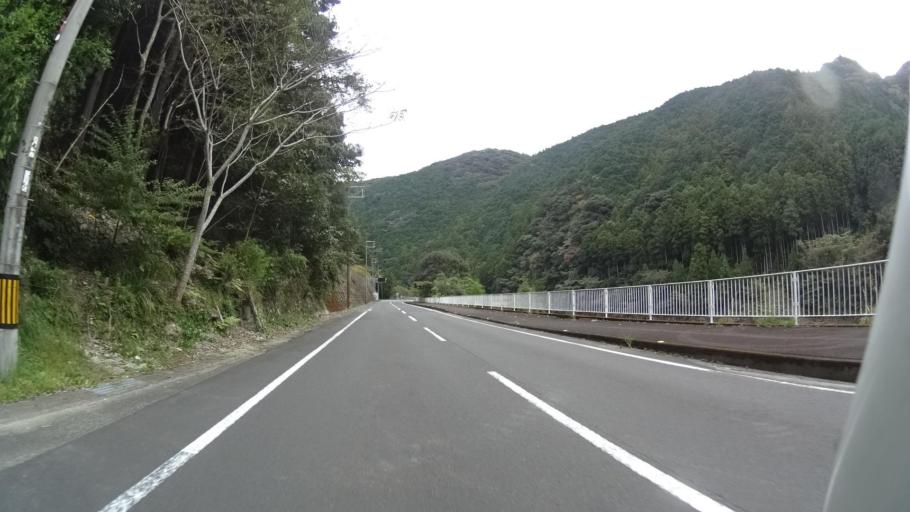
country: JP
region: Wakayama
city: Shingu
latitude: 33.5514
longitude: 135.7079
